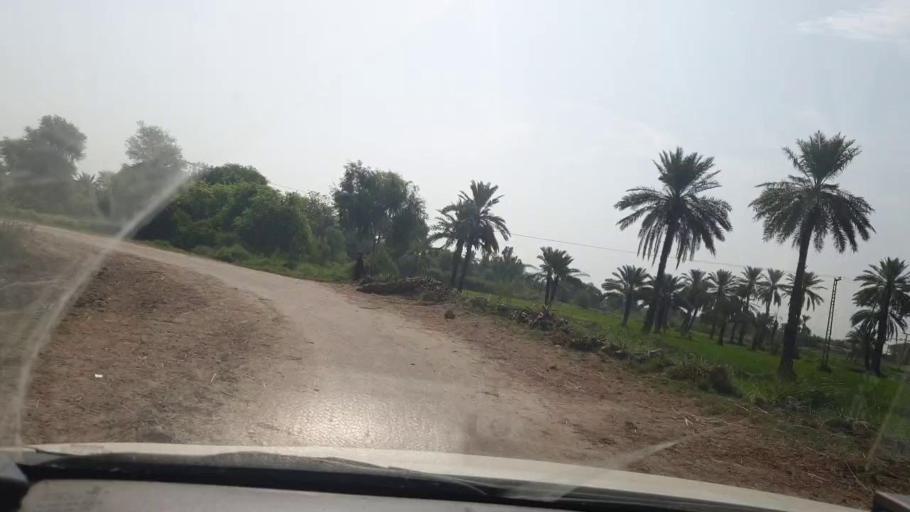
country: PK
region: Sindh
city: Chak
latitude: 27.8262
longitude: 68.7952
